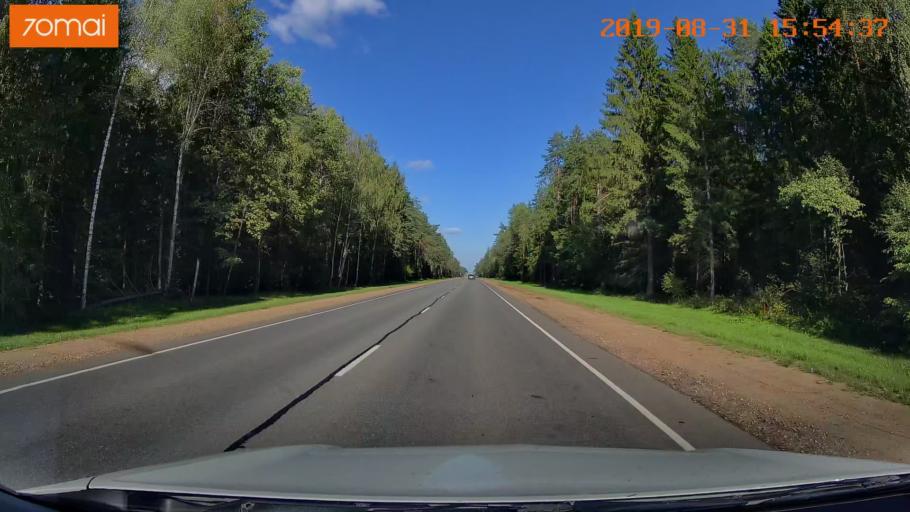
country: RU
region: Kaluga
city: Yukhnov
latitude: 54.7200
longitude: 35.1539
